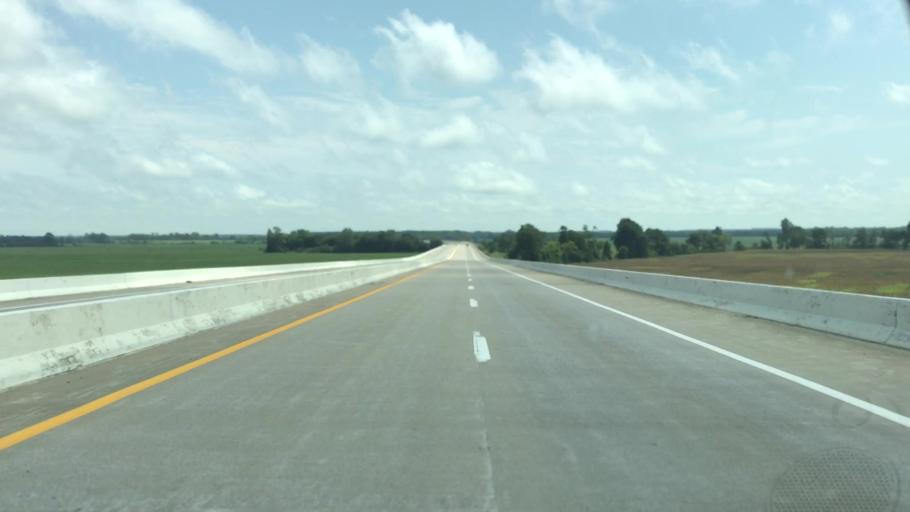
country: US
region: Missouri
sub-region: Pemiscot County
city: Caruthersville
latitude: 36.1096
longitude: -89.6100
